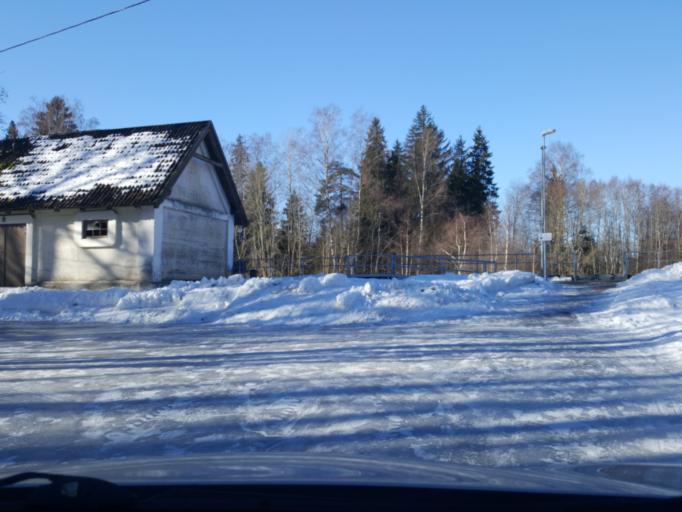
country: EE
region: Viljandimaa
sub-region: Suure-Jaani vald
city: Suure-Jaani
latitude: 58.5454
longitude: 25.5475
